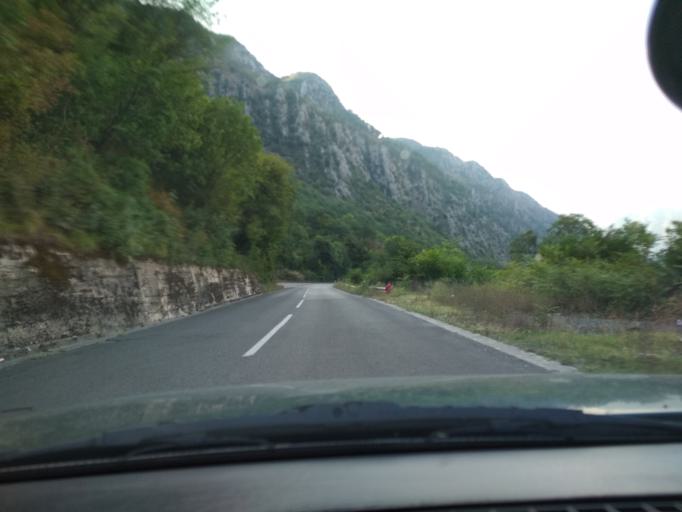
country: ME
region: Kotor
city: Kotor
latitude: 42.4124
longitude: 18.7631
